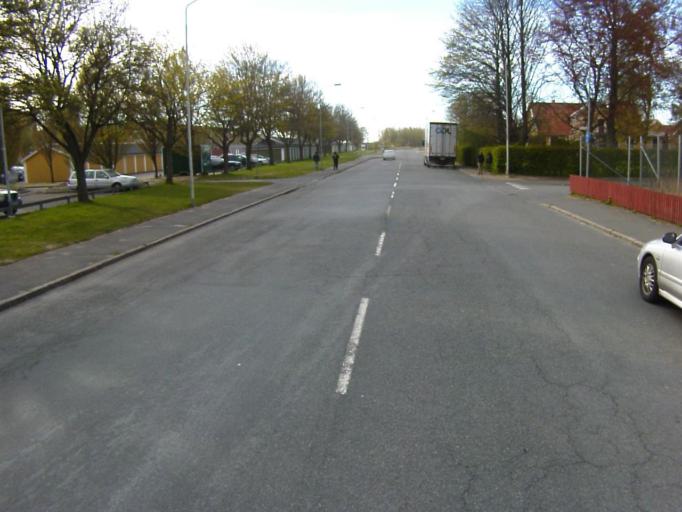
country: SE
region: Skane
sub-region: Kristianstads Kommun
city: Kristianstad
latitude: 56.0613
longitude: 14.1602
